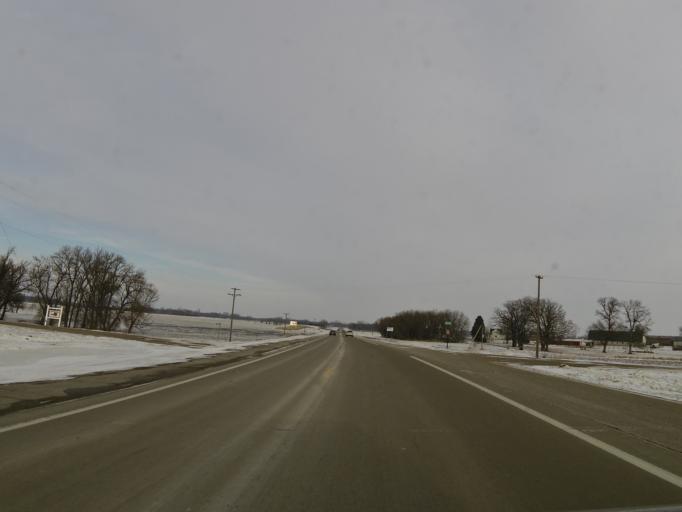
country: US
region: Minnesota
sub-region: McLeod County
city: Hutchinson
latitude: 44.8935
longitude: -94.2265
